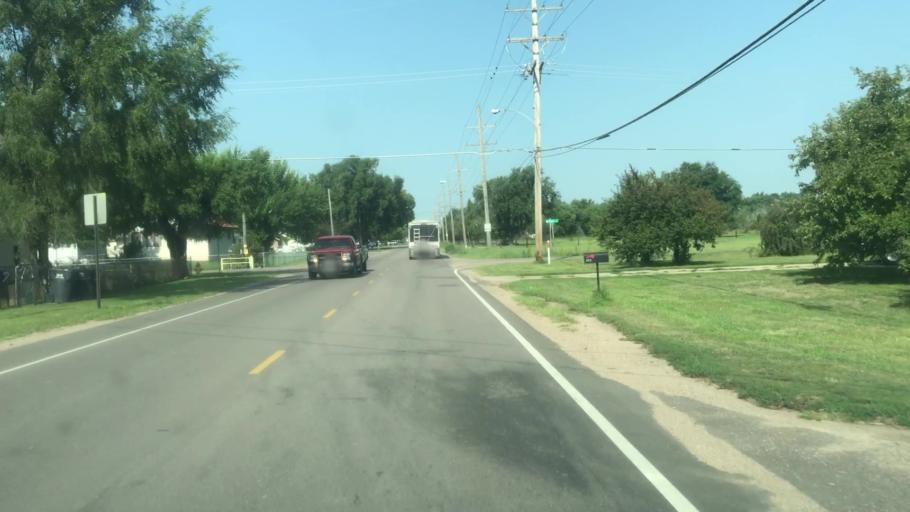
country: US
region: Nebraska
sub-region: Hall County
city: Grand Island
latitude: 40.9457
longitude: -98.3390
